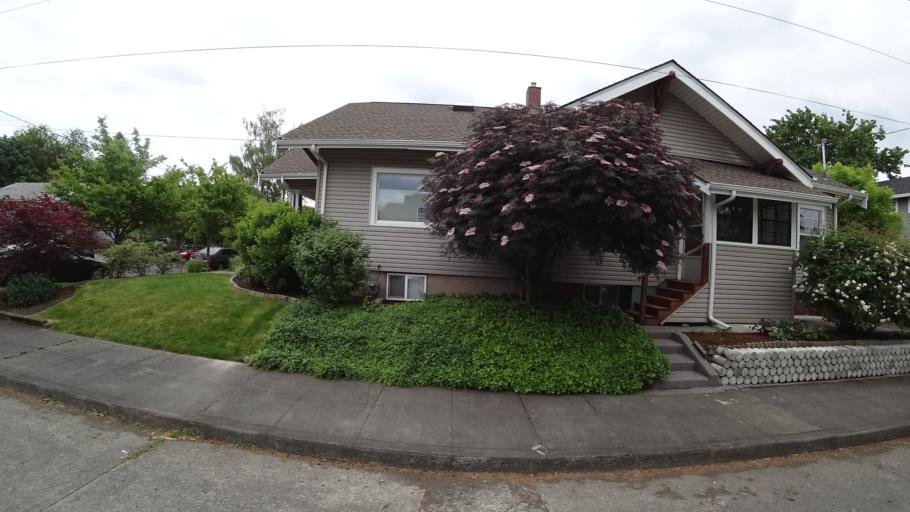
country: US
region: Oregon
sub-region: Multnomah County
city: Lents
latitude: 45.5066
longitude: -122.6145
